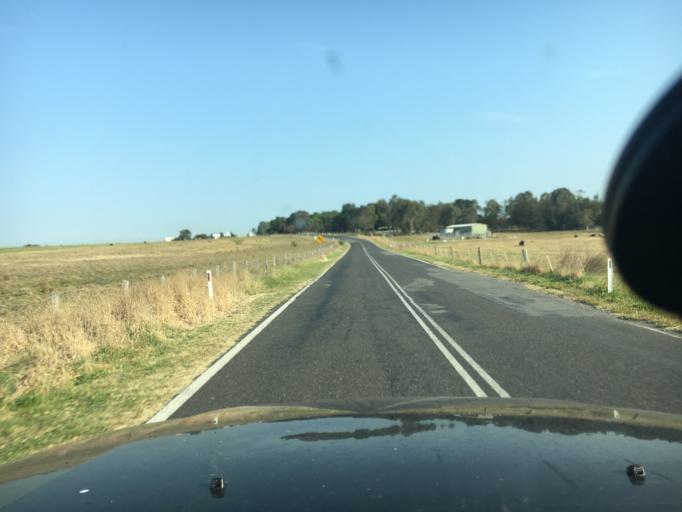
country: AU
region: New South Wales
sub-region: Cessnock
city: Branxton
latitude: -32.5889
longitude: 151.2858
